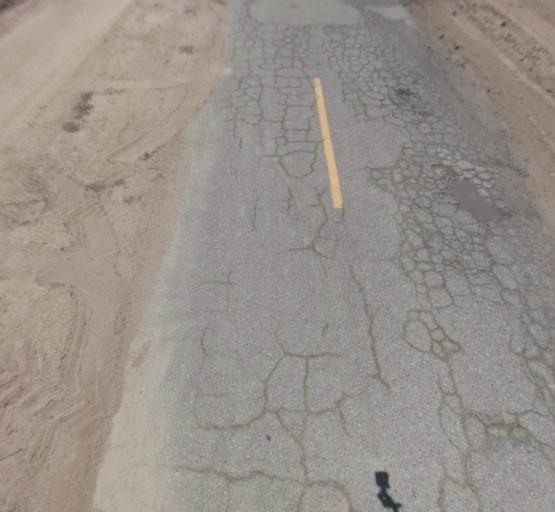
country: US
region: California
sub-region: Madera County
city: Chowchilla
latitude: 37.0703
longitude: -120.4191
